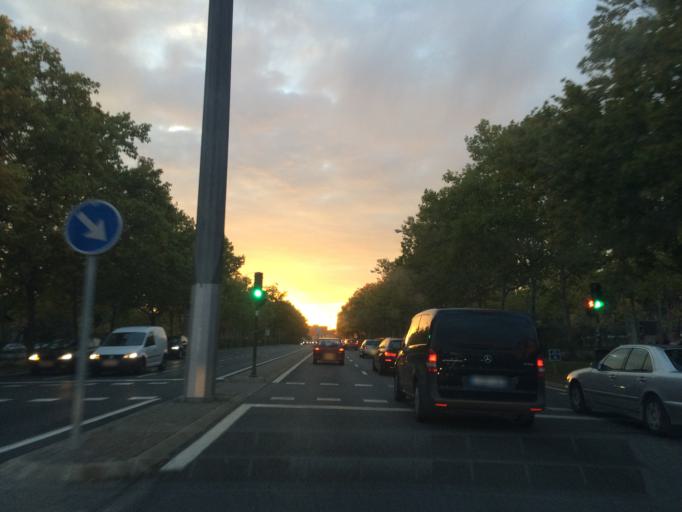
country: ES
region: Madrid
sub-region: Provincia de Madrid
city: Tetuan de las Victorias
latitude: 40.4819
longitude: -3.7055
